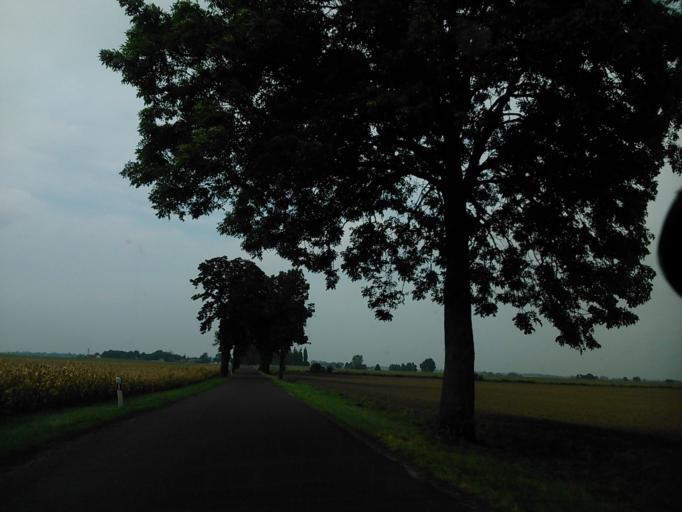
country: PL
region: Kujawsko-Pomorskie
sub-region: Powiat golubsko-dobrzynski
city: Kowalewo Pomorskie
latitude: 53.1887
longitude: 18.8319
